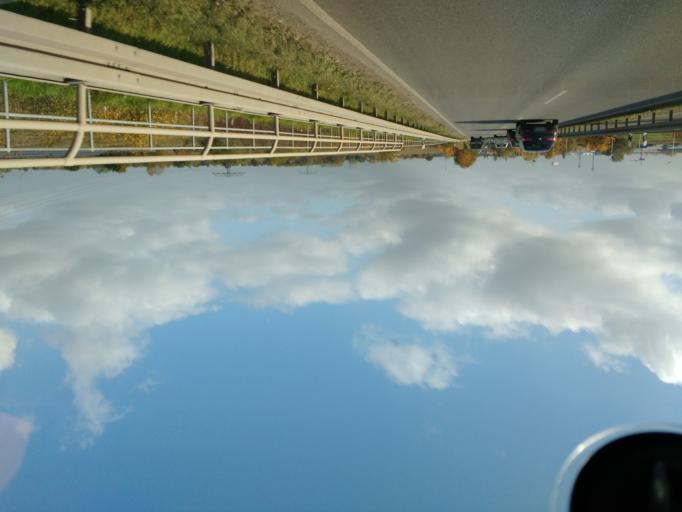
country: DE
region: Brandenburg
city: Petershagen
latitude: 52.4945
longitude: 13.7737
